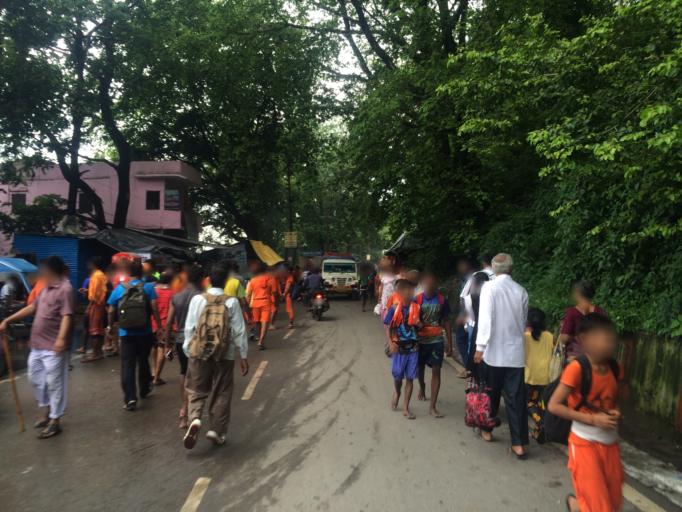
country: IN
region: Uttarakhand
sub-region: Dehradun
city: Rishikesh
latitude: 30.1202
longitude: 78.3070
